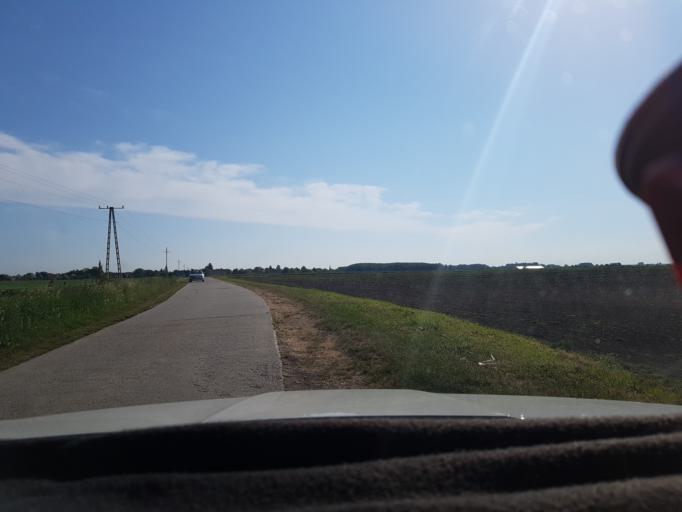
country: HU
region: Tolna
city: Decs
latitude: 46.2760
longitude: 18.7414
